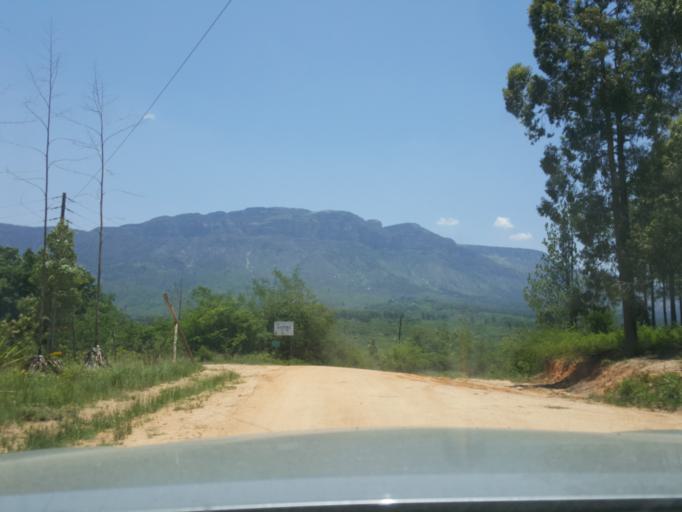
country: ZA
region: Limpopo
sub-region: Mopani District Municipality
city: Hoedspruit
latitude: -24.5926
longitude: 30.9402
